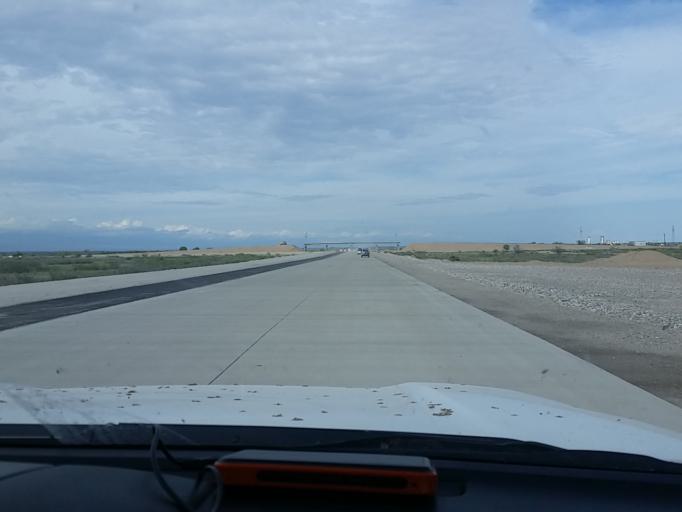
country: KZ
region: Almaty Oblysy
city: Zharkent
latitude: 44.0427
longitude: 79.9748
